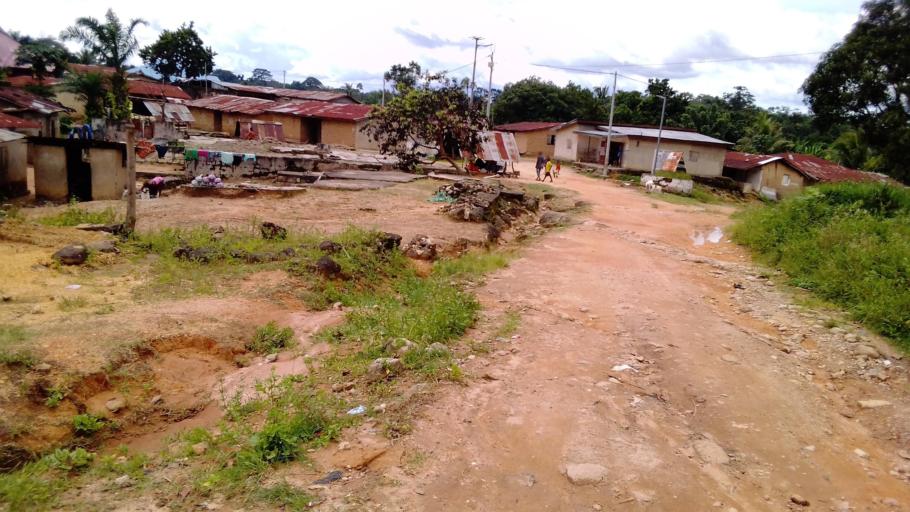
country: SL
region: Eastern Province
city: Koyima
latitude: 8.7009
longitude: -11.0090
